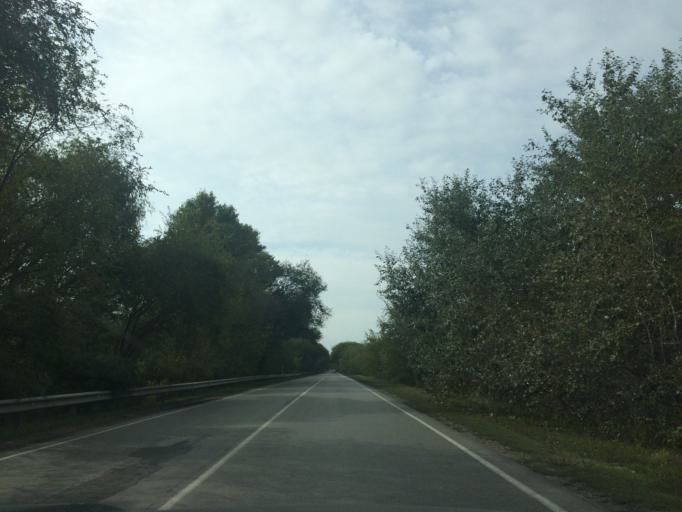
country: RU
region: Rostov
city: Kuleshovka
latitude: 47.1824
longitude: 39.6096
